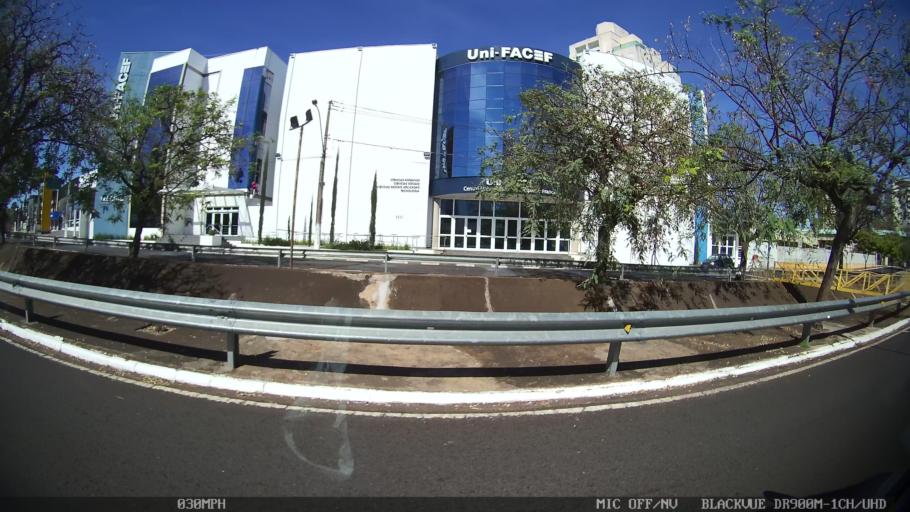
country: BR
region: Sao Paulo
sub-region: Franca
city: Franca
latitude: -20.5376
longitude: -47.3900
